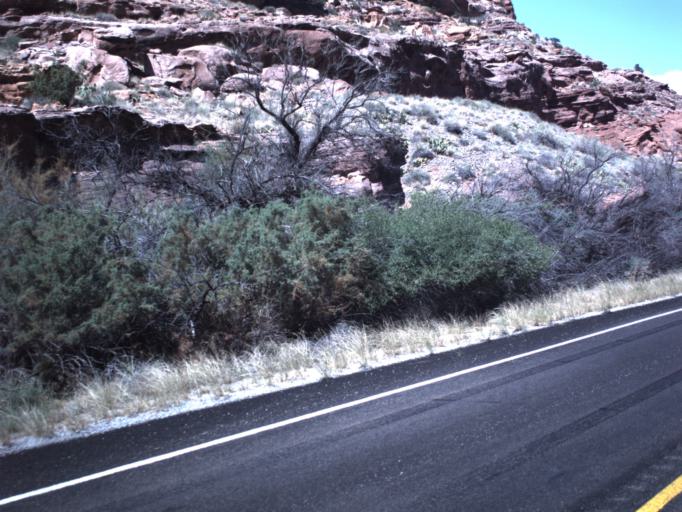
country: US
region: Utah
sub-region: Grand County
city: Moab
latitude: 38.5604
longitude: -109.5860
